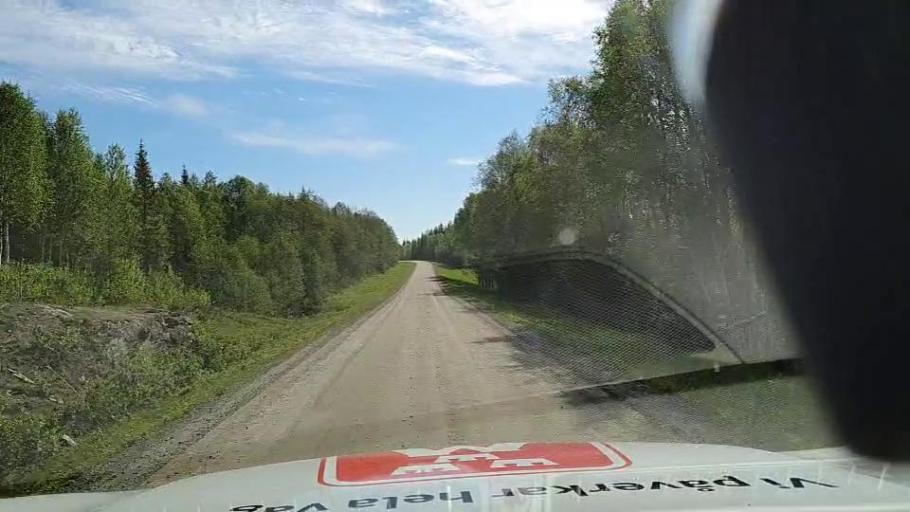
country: NO
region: Nord-Trondelag
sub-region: Lierne
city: Sandvika
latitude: 64.5876
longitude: 13.8314
